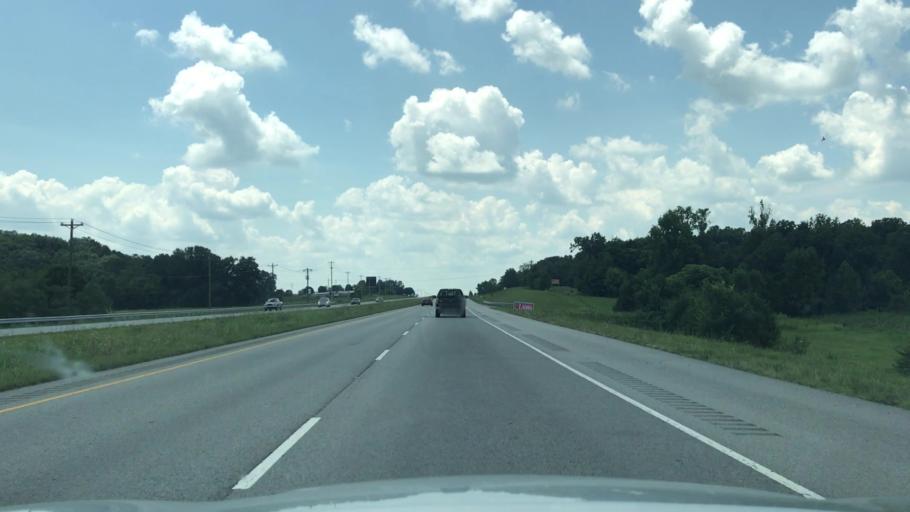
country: US
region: Tennessee
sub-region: Overton County
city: Livingston
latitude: 36.3039
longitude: -85.3675
